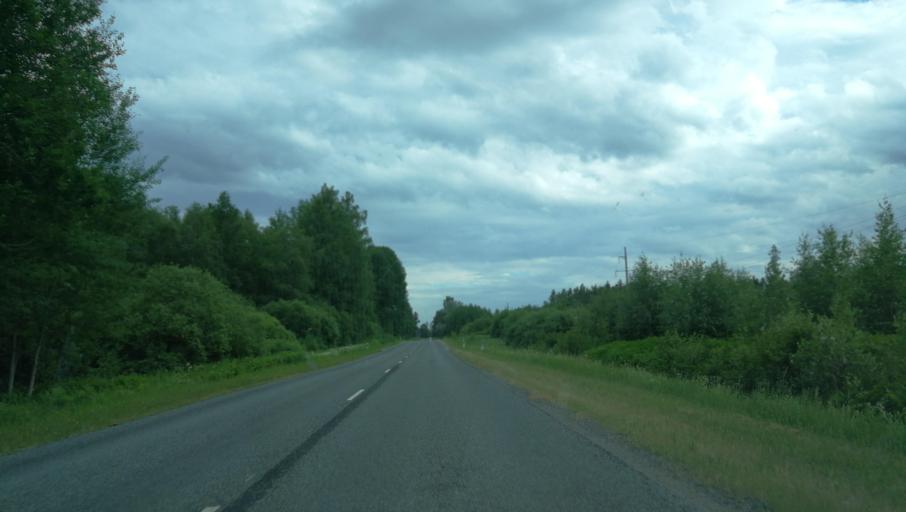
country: LV
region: Naukseni
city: Naukseni
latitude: 57.7838
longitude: 25.4260
